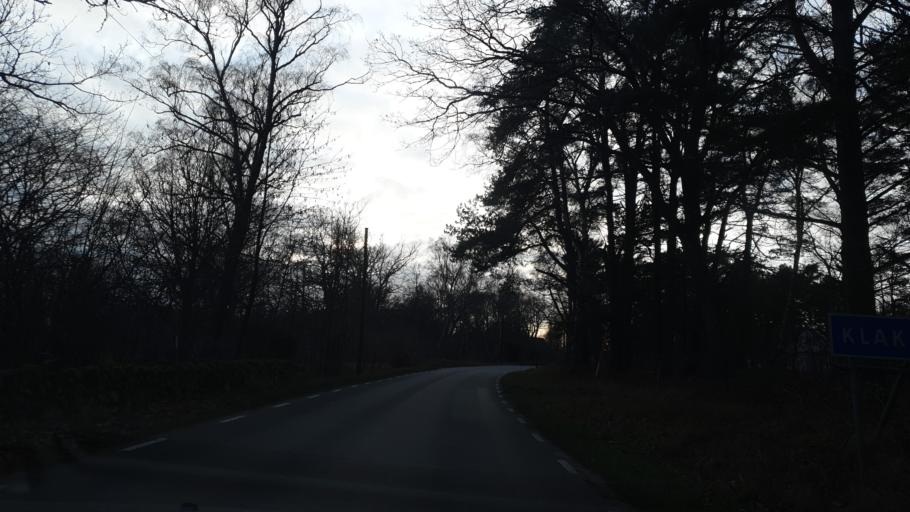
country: SE
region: Blekinge
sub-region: Karlskrona Kommun
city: Jaemjoe
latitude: 56.2009
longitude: 15.9550
